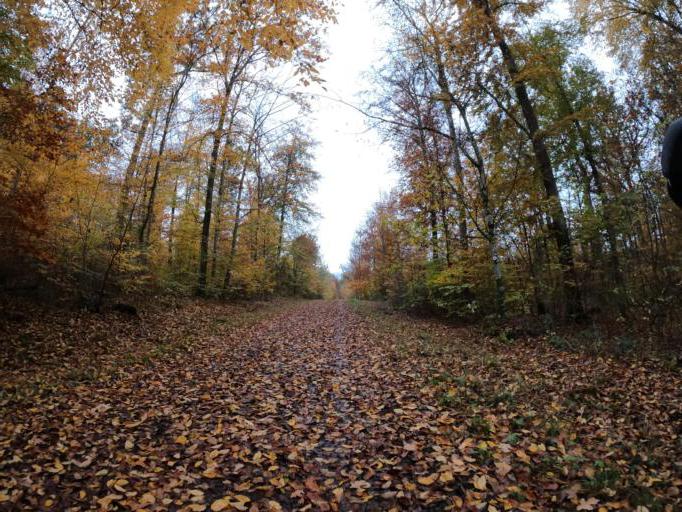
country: DE
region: Baden-Wuerttemberg
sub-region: Regierungsbezirk Stuttgart
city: Ehningen
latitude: 48.6419
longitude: 8.9482
